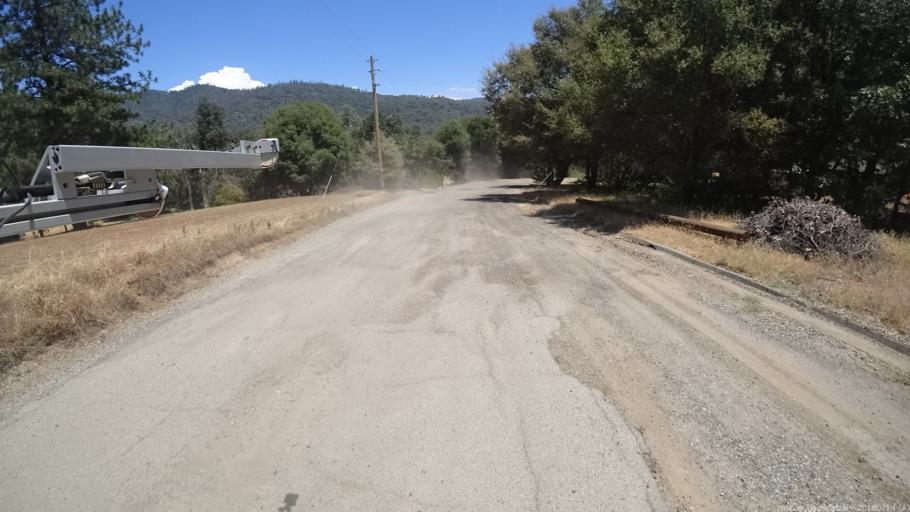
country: US
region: California
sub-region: Madera County
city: Ahwahnee
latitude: 37.4100
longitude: -119.7216
